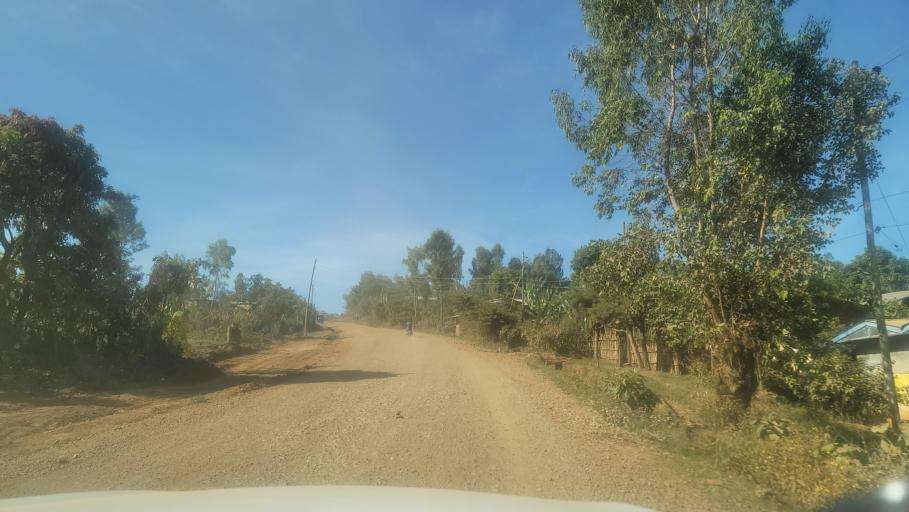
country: ET
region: Oromiya
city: Agaro
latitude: 7.8218
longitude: 36.5287
